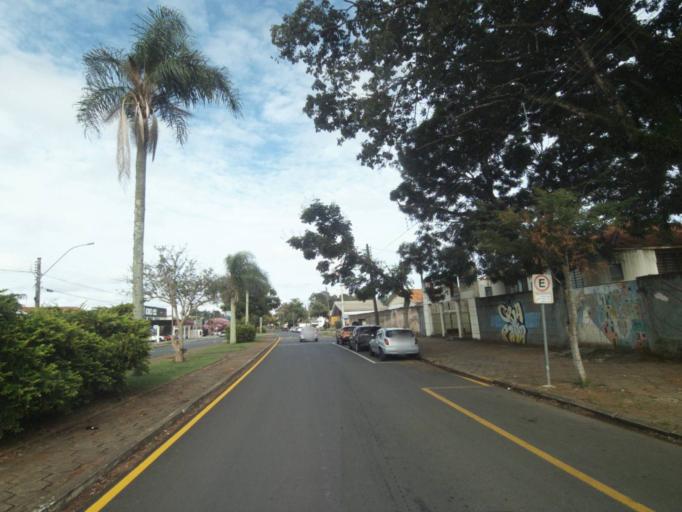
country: BR
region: Parana
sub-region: Telemaco Borba
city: Telemaco Borba
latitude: -24.3296
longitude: -50.6168
